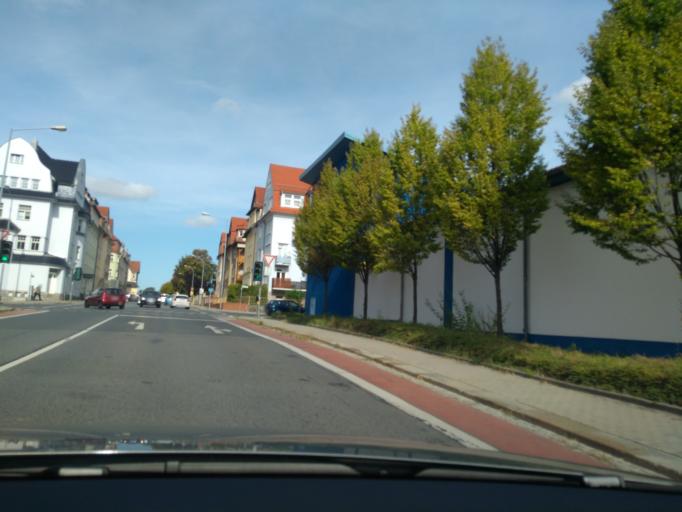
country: DE
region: Saxony
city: Bautzen
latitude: 51.1708
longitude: 14.4351
